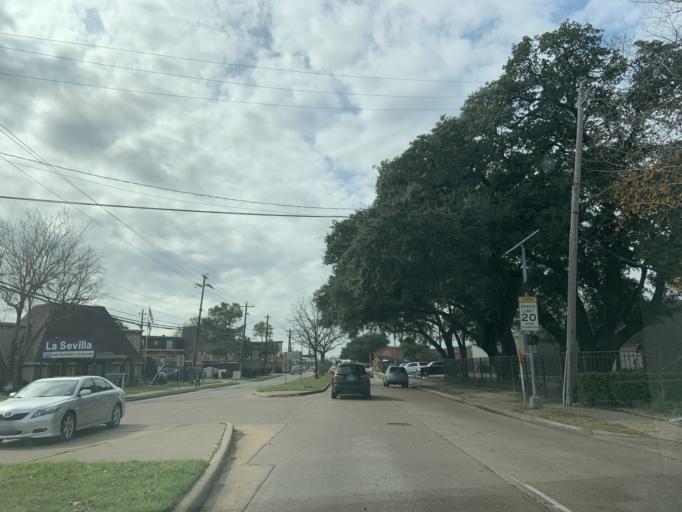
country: US
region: Texas
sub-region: Harris County
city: Bellaire
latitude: 29.6988
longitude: -95.4854
